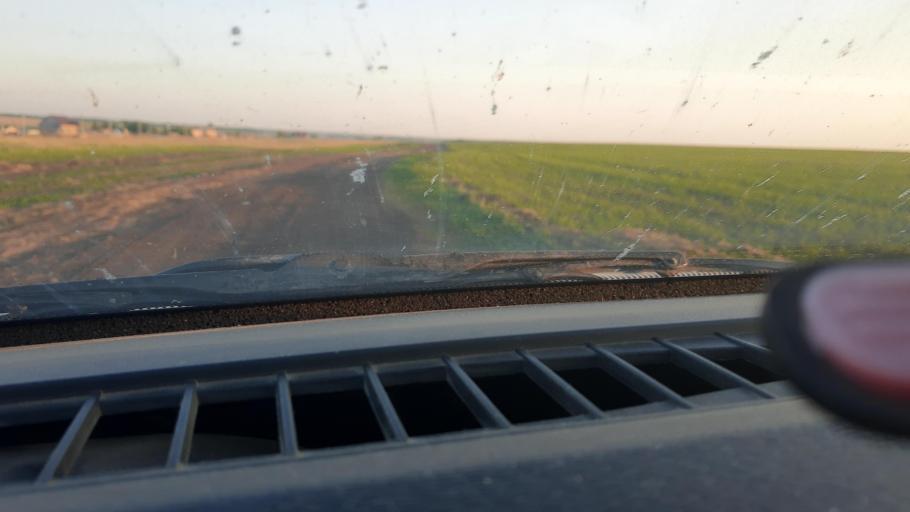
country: RU
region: Bashkortostan
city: Asanovo
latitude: 54.8608
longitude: 55.5890
